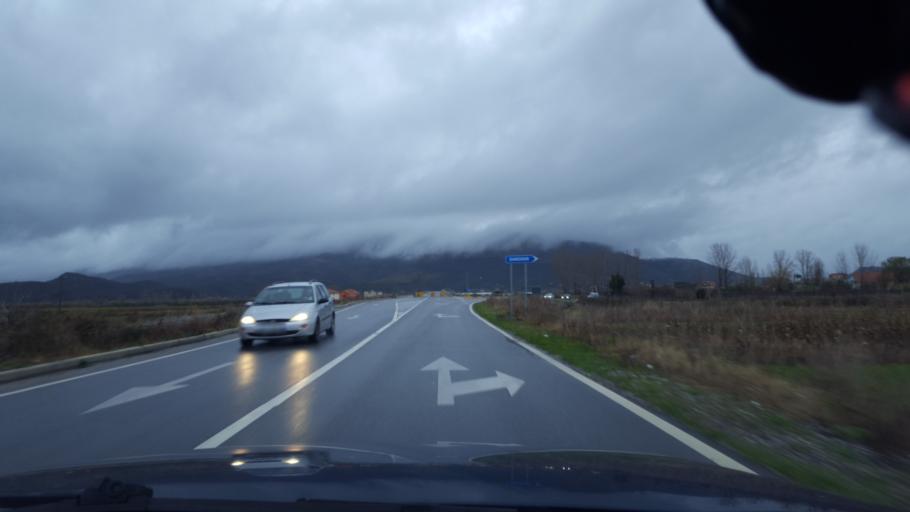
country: AL
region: Shkoder
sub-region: Rrethi i Shkodres
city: Berdica e Madhe
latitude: 42.0047
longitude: 19.4799
